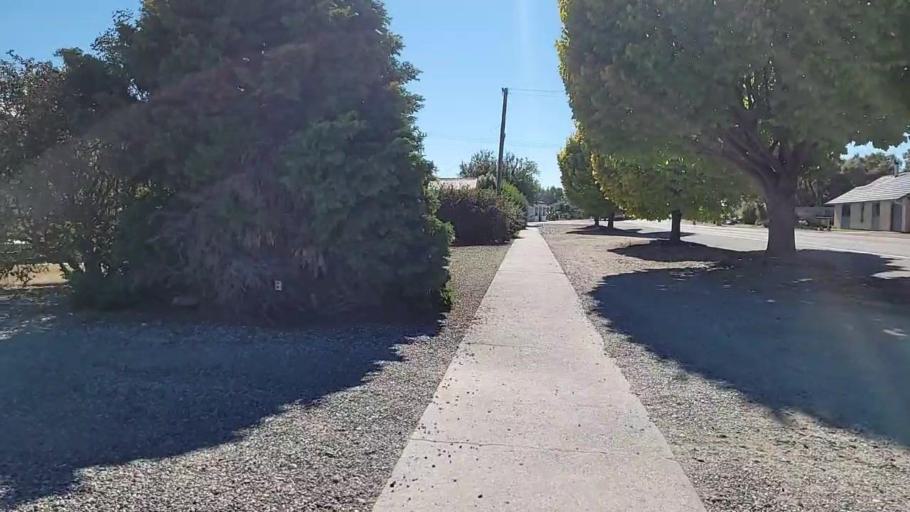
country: NZ
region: Otago
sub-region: Queenstown-Lakes District
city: Wanaka
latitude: -45.0971
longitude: 169.5987
